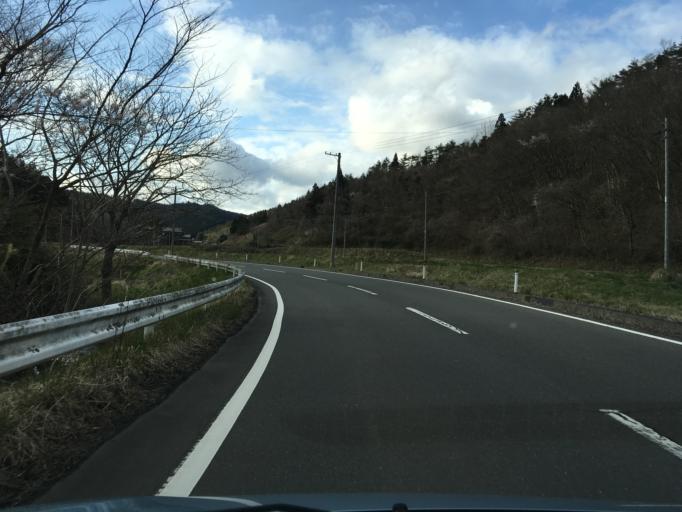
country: JP
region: Iwate
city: Ichinoseki
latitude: 38.7952
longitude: 141.3204
